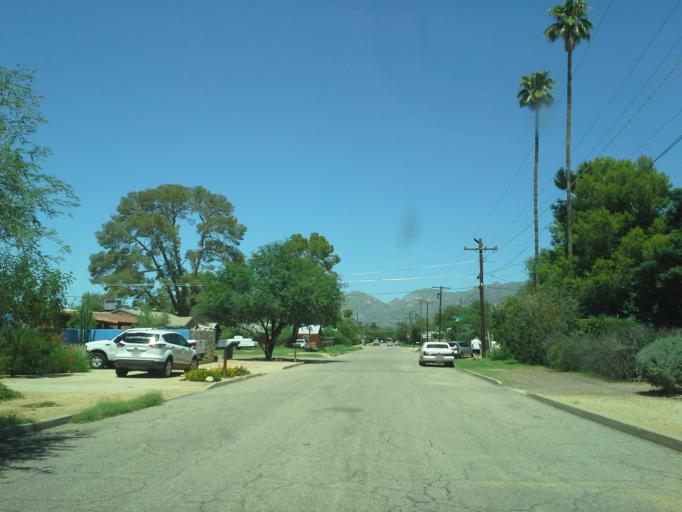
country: US
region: Arizona
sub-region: Pima County
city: Tucson
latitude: 32.2542
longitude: -110.9332
